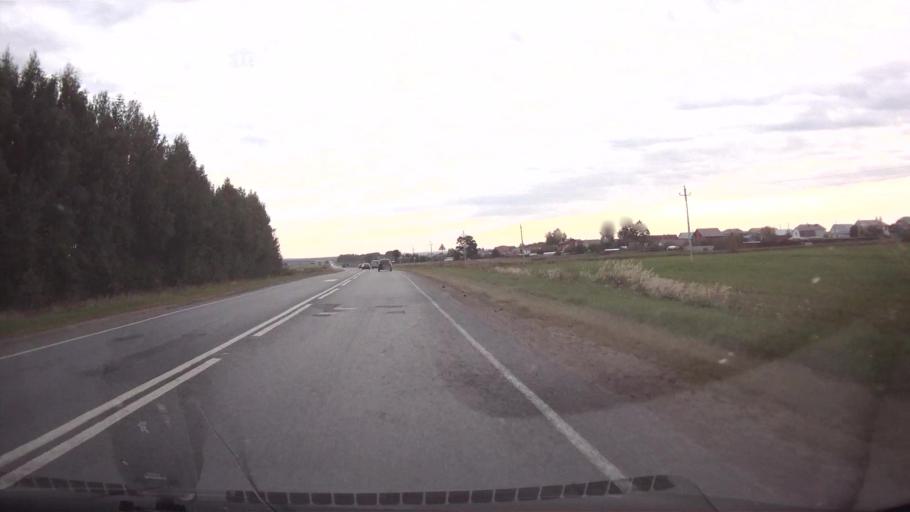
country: RU
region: Mariy-El
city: Yoshkar-Ola
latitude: 56.7156
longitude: 48.0956
